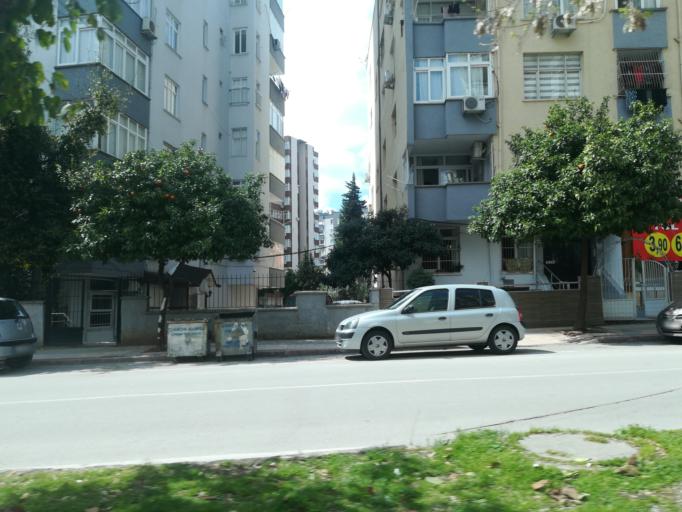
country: TR
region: Adana
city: Adana
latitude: 37.0414
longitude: 35.3020
